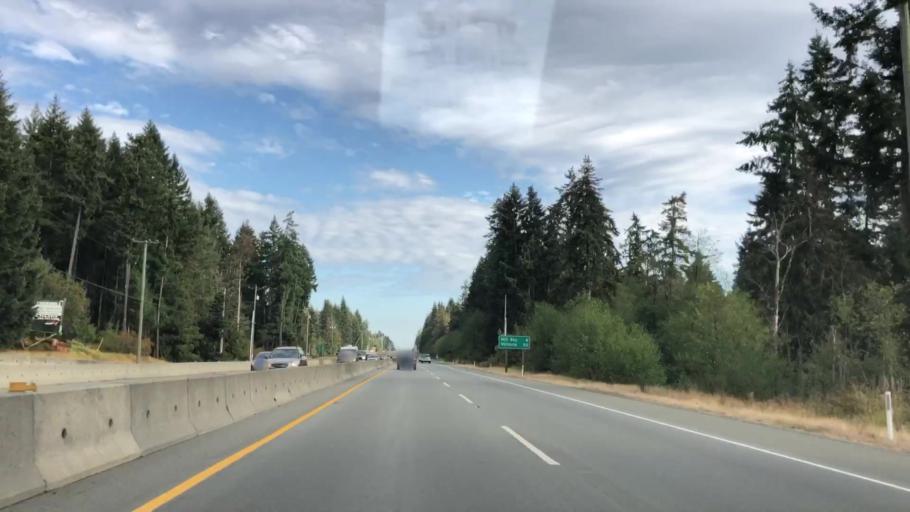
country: CA
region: British Columbia
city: Duncan
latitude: 48.7026
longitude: -123.6008
